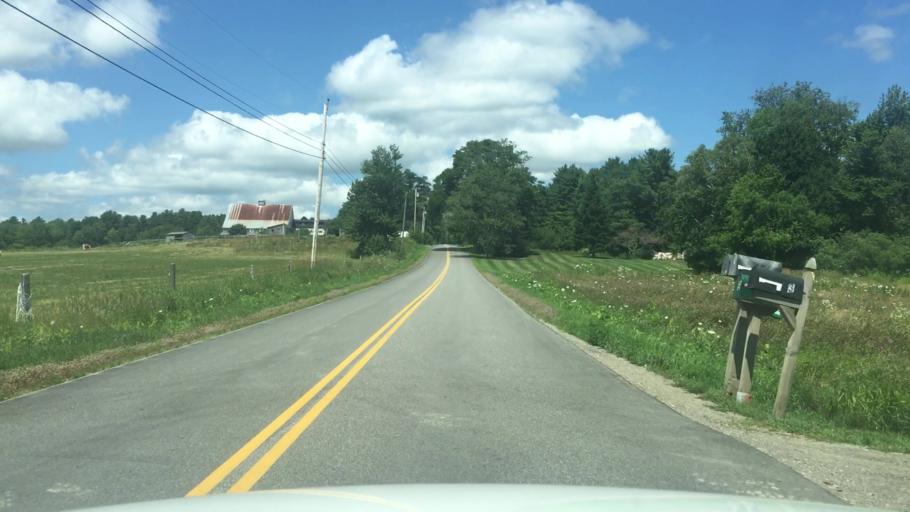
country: US
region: Maine
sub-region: Waldo County
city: Belfast
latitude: 44.4094
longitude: -69.0357
